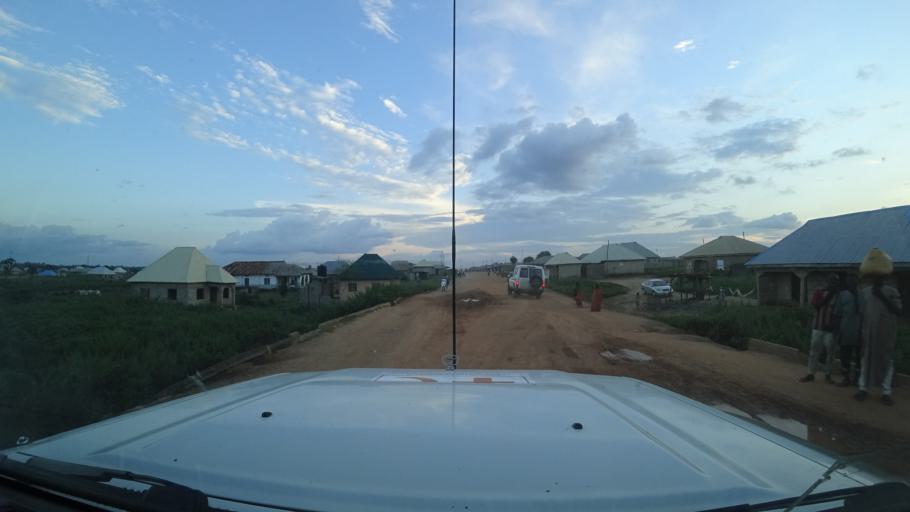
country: NG
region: Niger
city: Minna
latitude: 9.6448
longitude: 6.5809
